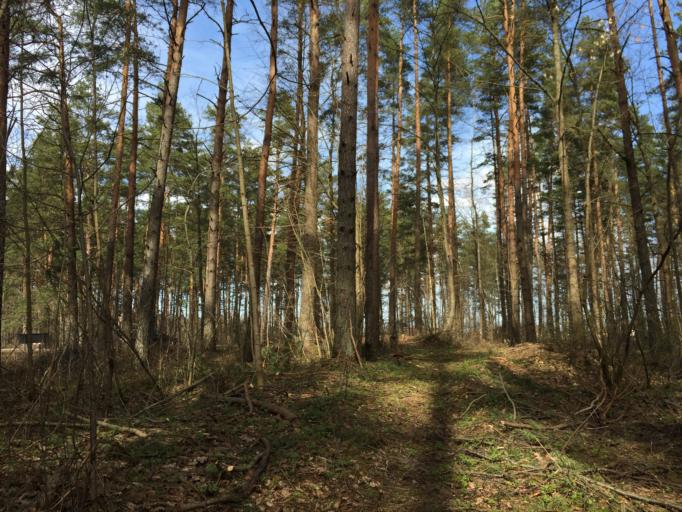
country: LV
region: Salaspils
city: Salaspils
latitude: 56.8839
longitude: 24.3623
